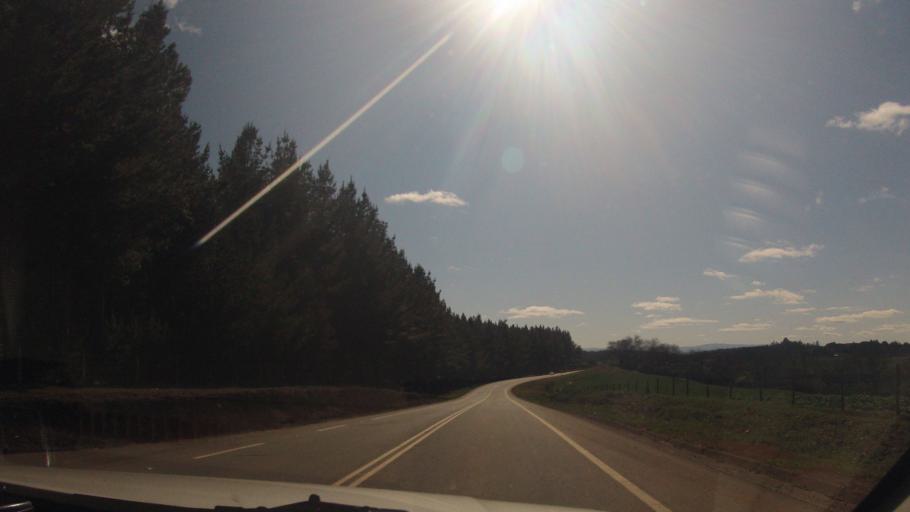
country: CL
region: Araucania
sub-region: Provincia de Malleco
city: Traiguen
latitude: -38.2000
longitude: -72.8010
